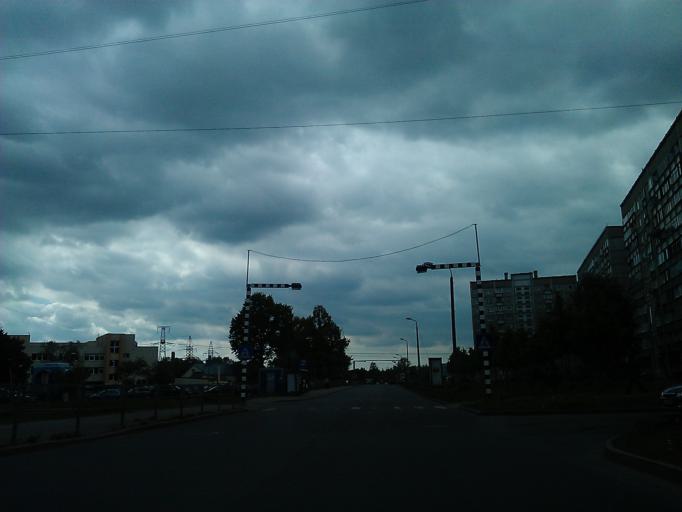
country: LV
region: Kekava
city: Balozi
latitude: 56.9009
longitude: 24.0928
